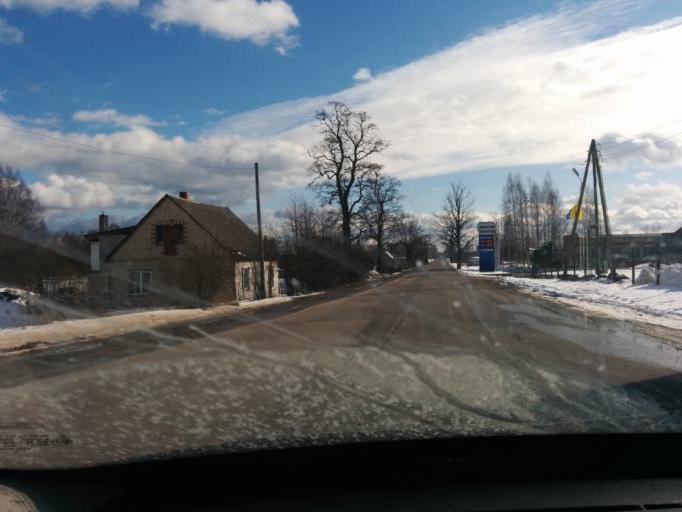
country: LV
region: Gulbenes Rajons
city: Gulbene
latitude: 57.1835
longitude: 26.7371
